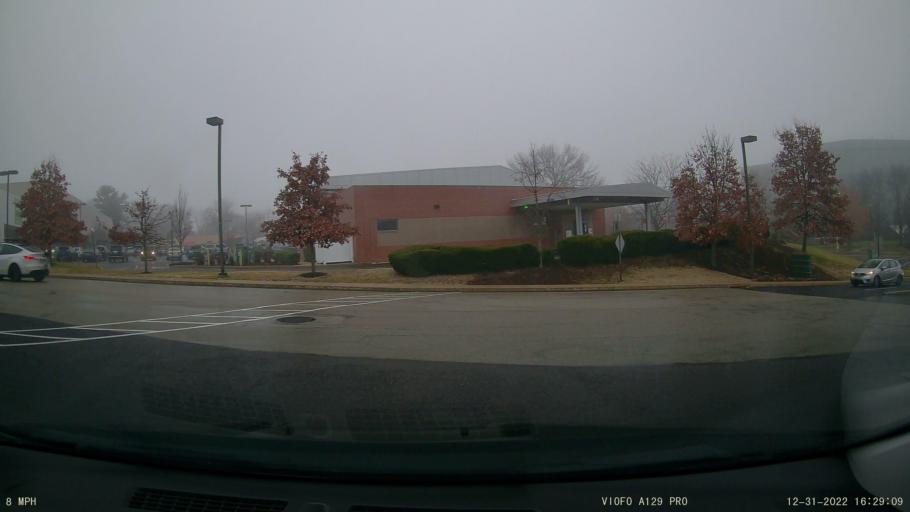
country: US
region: Pennsylvania
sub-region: Delaware County
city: Radnor
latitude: 40.0401
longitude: -75.3685
